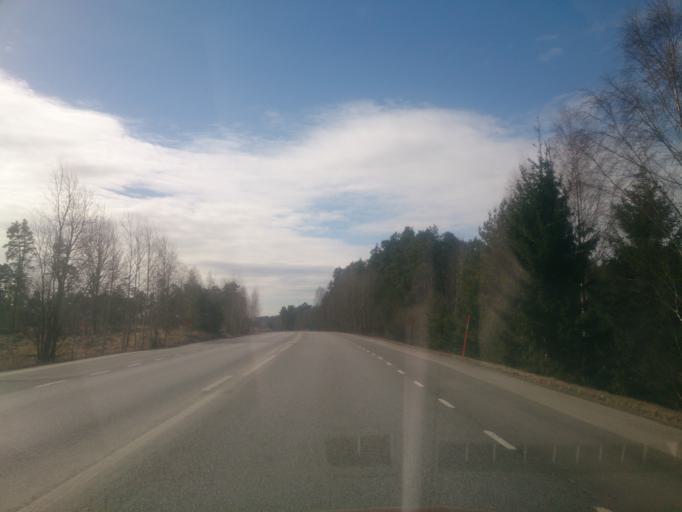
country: SE
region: OEstergoetland
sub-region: Norrkopings Kommun
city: Kimstad
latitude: 58.4941
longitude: 15.9553
